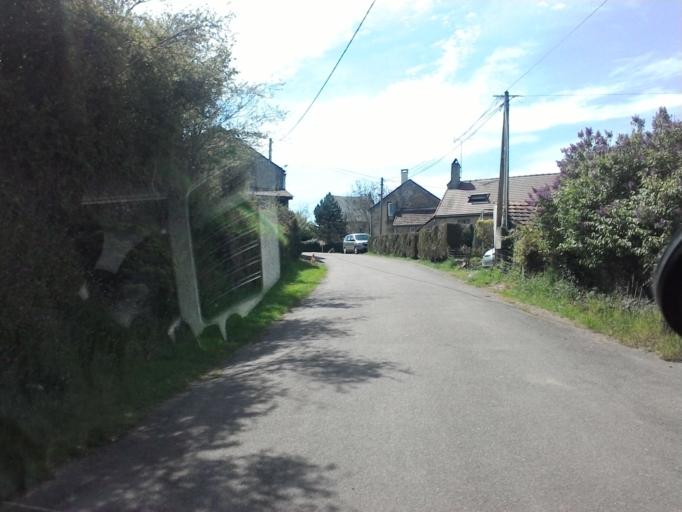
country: FR
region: Bourgogne
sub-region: Departement de la Nievre
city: Lormes
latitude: 47.3388
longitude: 3.9113
